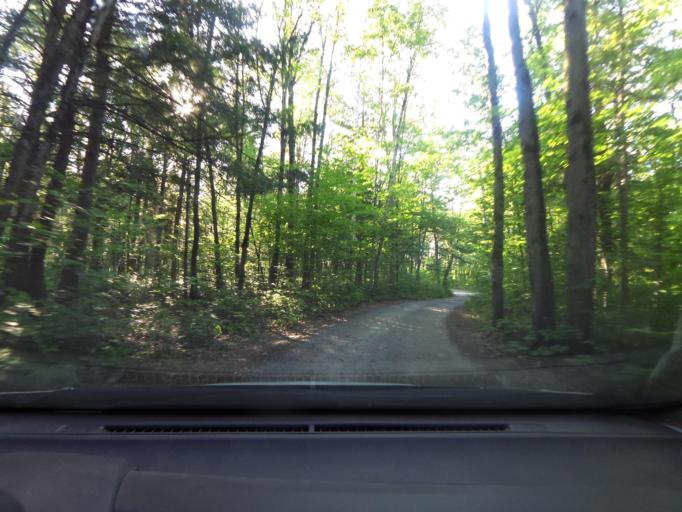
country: CA
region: Quebec
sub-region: Mauricie
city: Becancour
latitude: 46.5458
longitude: -72.4060
